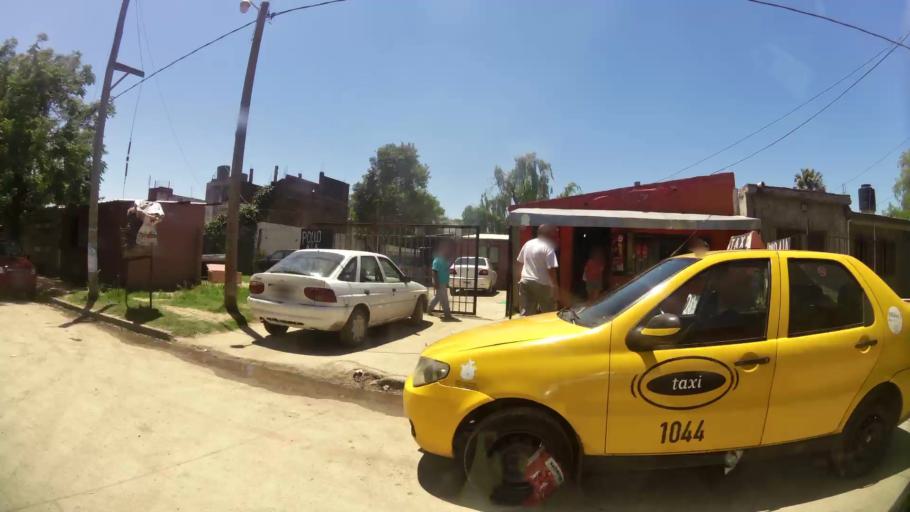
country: AR
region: Cordoba
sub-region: Departamento de Capital
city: Cordoba
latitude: -31.4168
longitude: -64.2356
